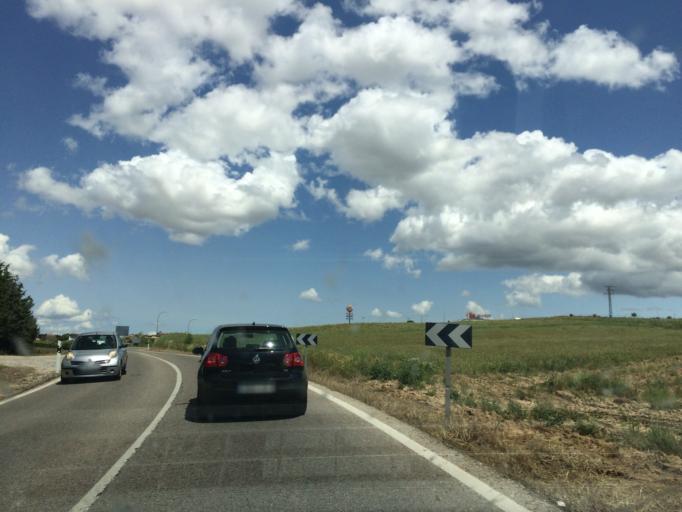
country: ES
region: Madrid
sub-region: Provincia de Madrid
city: Valdeolmos
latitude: 40.6870
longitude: -3.4587
